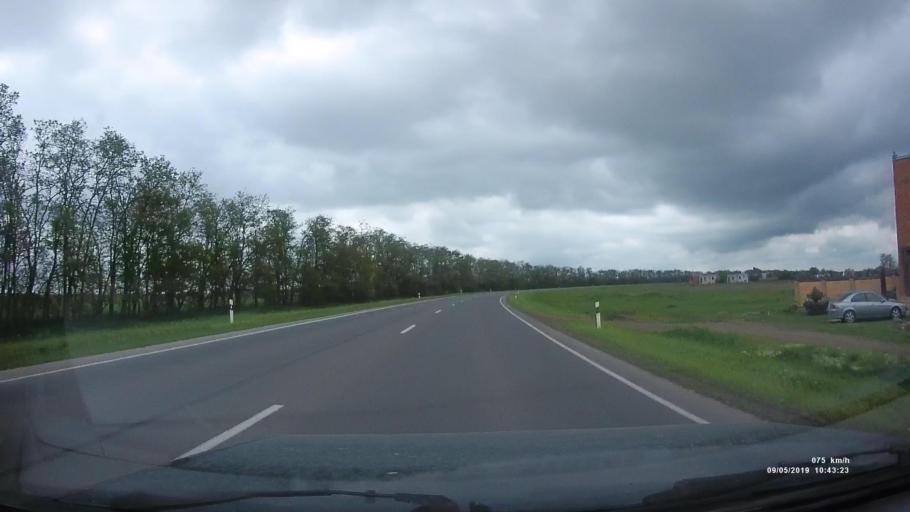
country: RU
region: Rostov
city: Peshkovo
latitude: 47.0087
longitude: 39.4036
